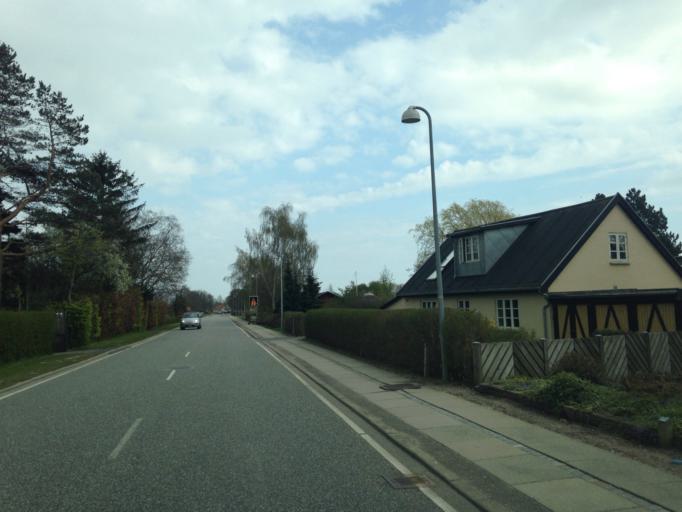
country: DK
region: Capital Region
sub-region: Hoje-Taastrup Kommune
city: Taastrup
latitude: 55.6281
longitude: 12.2912
